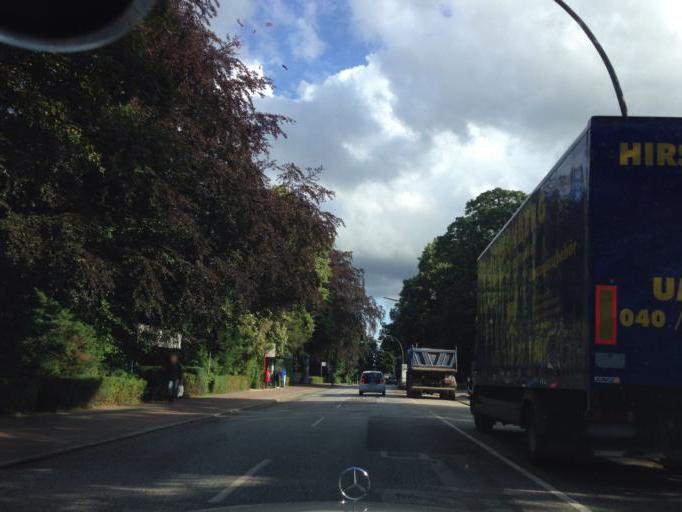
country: DE
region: Hamburg
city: Farmsen-Berne
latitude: 53.6145
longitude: 10.1146
